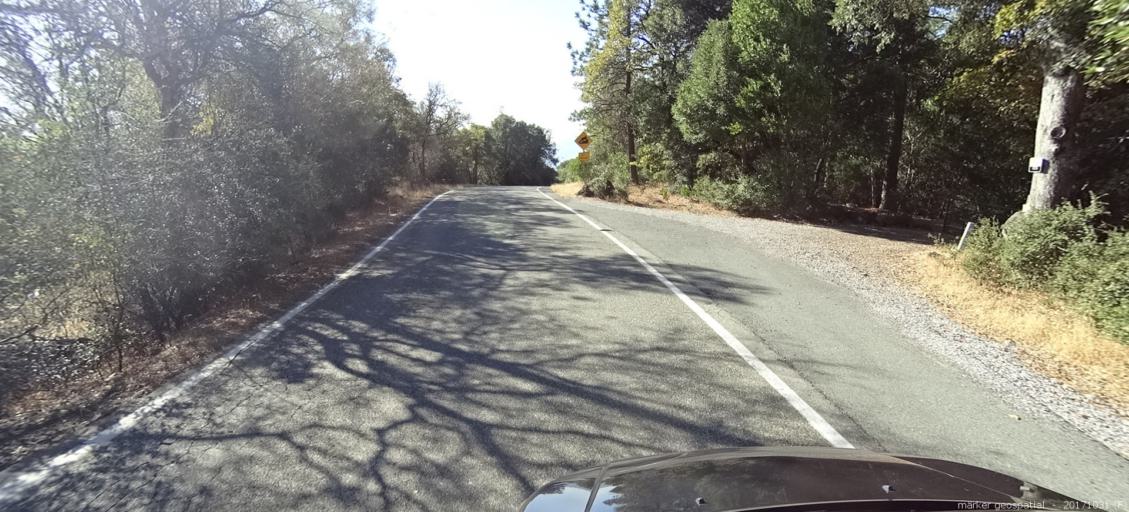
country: US
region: California
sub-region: Shasta County
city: Shingletown
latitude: 40.4645
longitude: -121.8871
